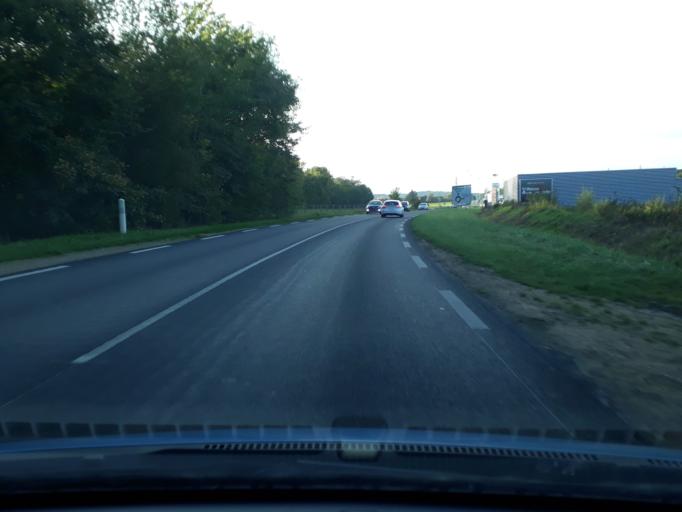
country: FR
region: Ile-de-France
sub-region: Departement de Seine-et-Marne
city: Vulaines-sur-Seine
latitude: 48.4214
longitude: 2.7734
